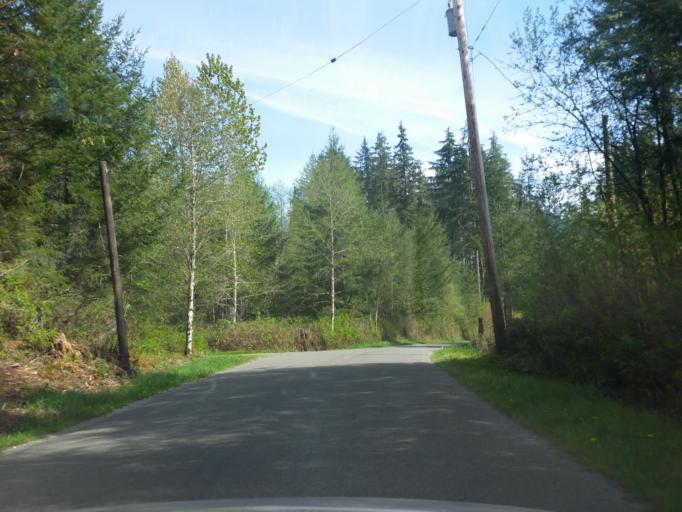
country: US
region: Washington
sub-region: Snohomish County
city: Woods Creek
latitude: 47.9808
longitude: -121.8876
